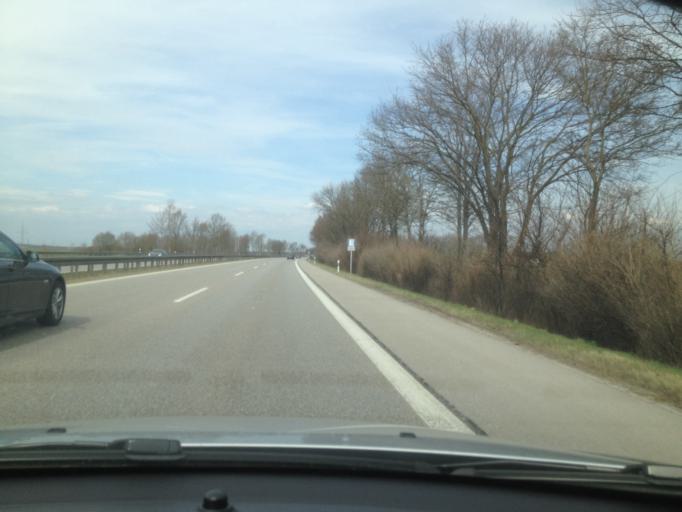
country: DE
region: Bavaria
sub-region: Swabia
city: Konigsbrunn
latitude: 48.2658
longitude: 10.8668
